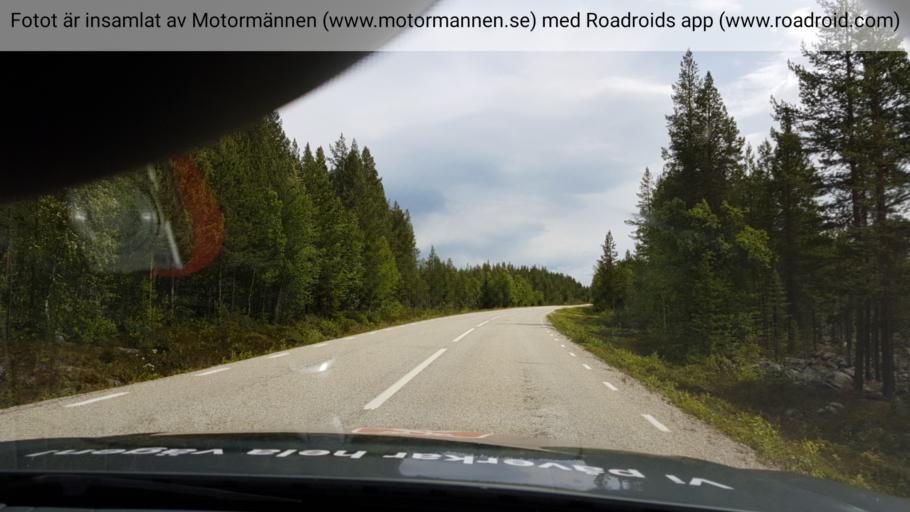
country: SE
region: Jaemtland
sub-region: Are Kommun
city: Jarpen
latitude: 62.8226
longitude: 13.5016
